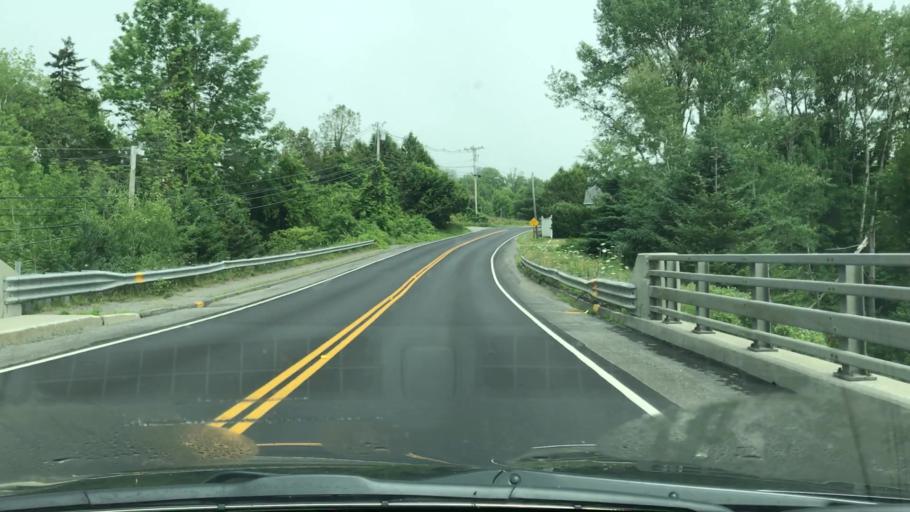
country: US
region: Maine
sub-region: Waldo County
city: Lincolnville
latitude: 44.2977
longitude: -69.0046
